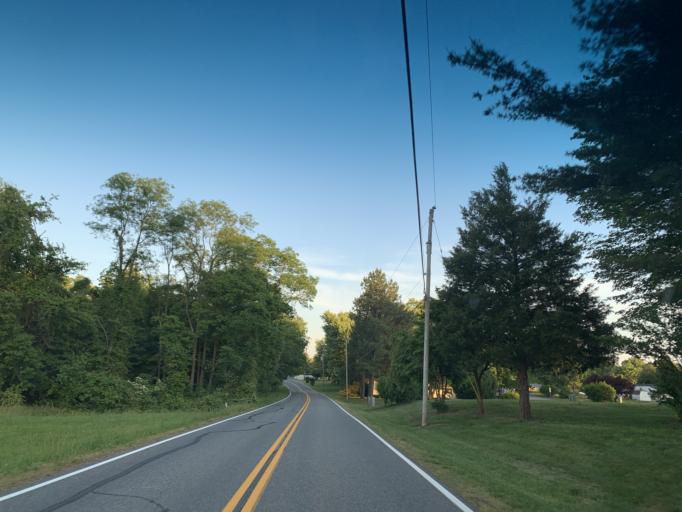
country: US
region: Maryland
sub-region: Cecil County
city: Rising Sun
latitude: 39.6292
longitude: -76.0677
